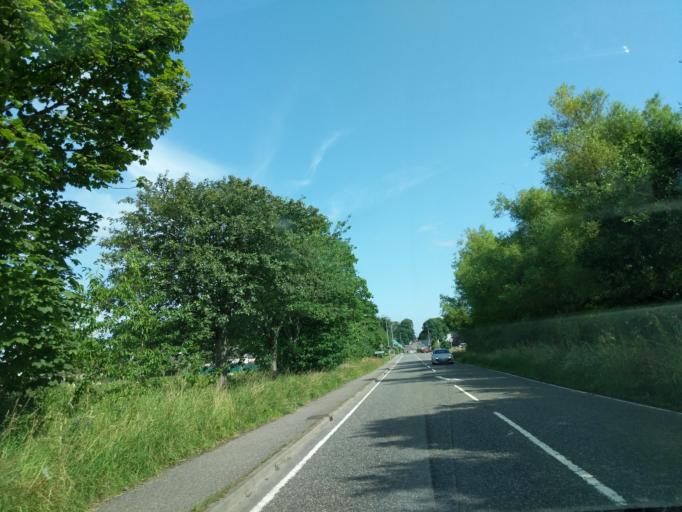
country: GB
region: Scotland
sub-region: Moray
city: Lhanbryd
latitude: 57.6359
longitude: -3.2278
